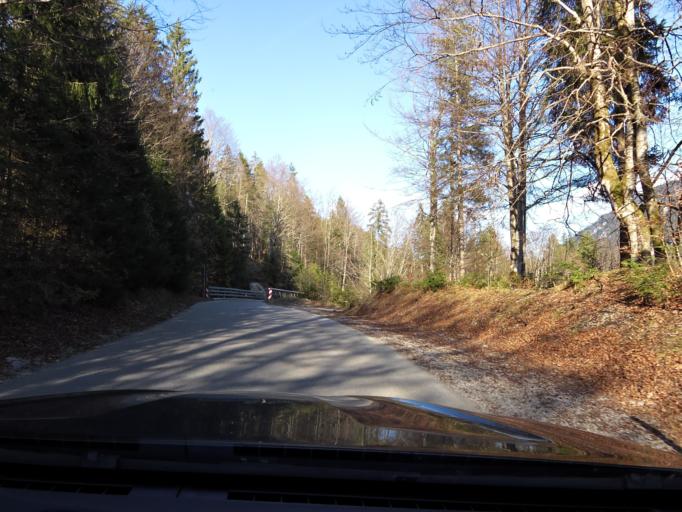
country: DE
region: Bavaria
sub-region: Upper Bavaria
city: Wallgau
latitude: 47.5446
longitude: 11.3608
